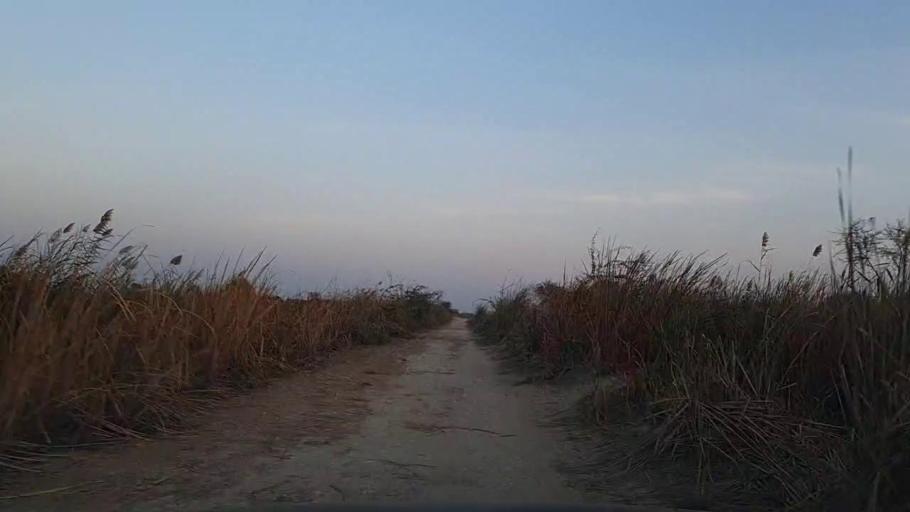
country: PK
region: Sindh
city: Tando Mittha Khan
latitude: 25.9433
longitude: 69.1326
